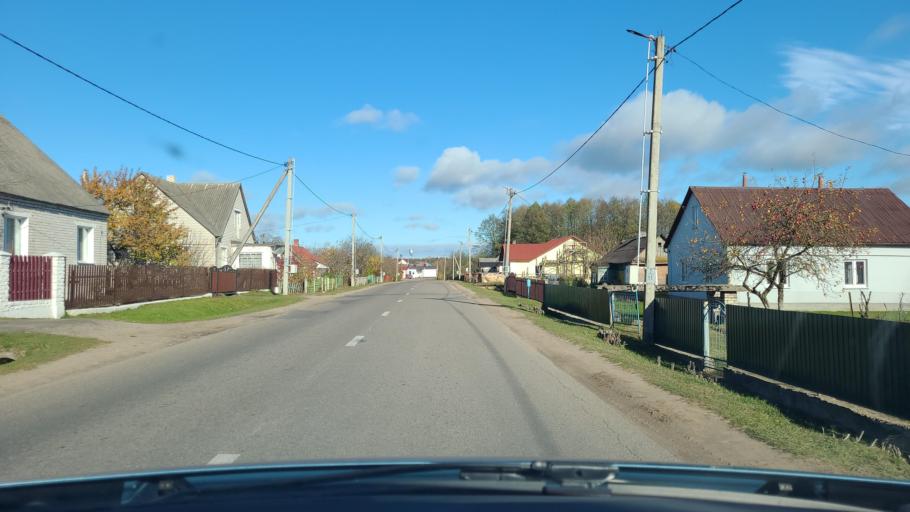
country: BY
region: Grodnenskaya
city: Astravyets
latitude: 54.6106
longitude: 25.9488
